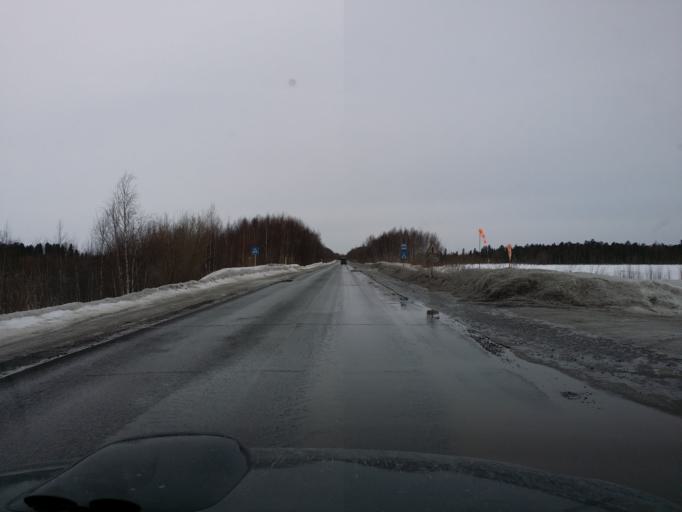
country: RU
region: Tomsk
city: Strezhevoy
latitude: 60.7414
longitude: 77.5329
